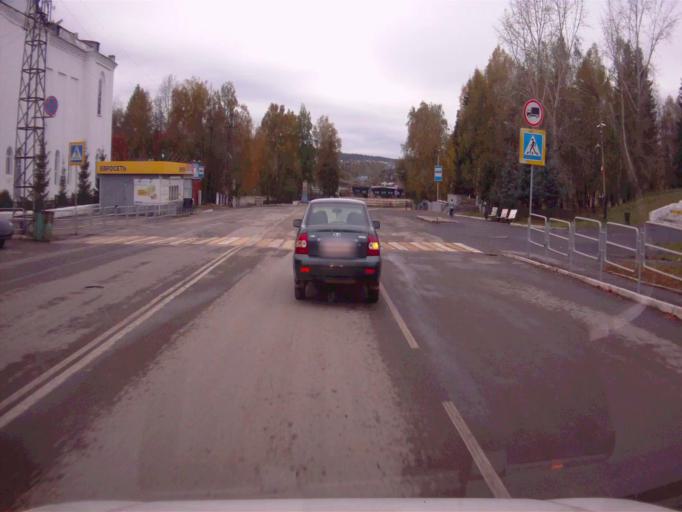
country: RU
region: Chelyabinsk
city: Nyazepetrovsk
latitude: 56.0538
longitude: 59.5962
